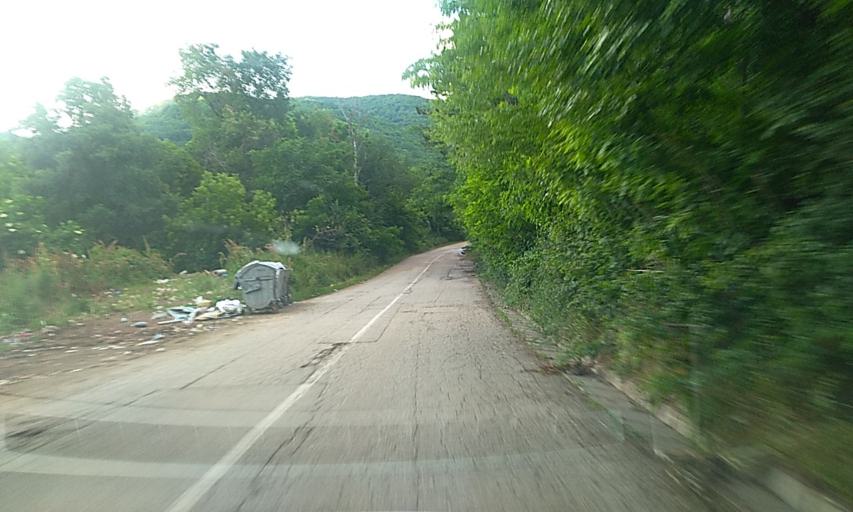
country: RS
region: Central Serbia
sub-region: Nisavski Okrug
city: Niska Banja
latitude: 43.3678
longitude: 21.9882
